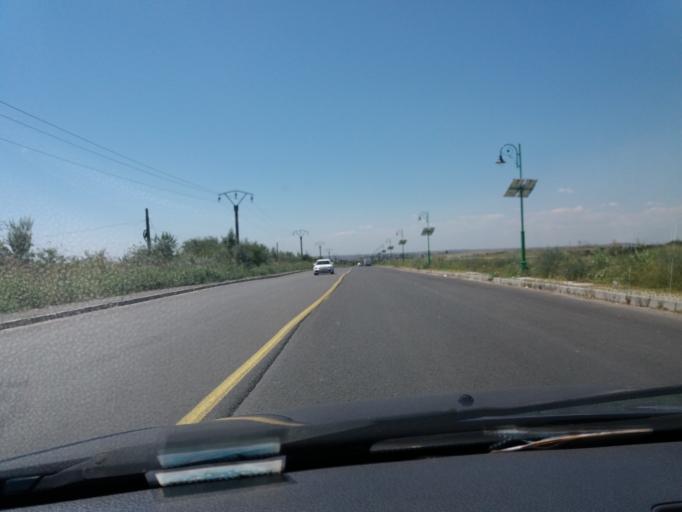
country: RO
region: Constanta
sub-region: Comuna Navodari
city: Navodari
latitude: 44.2903
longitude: 28.6092
